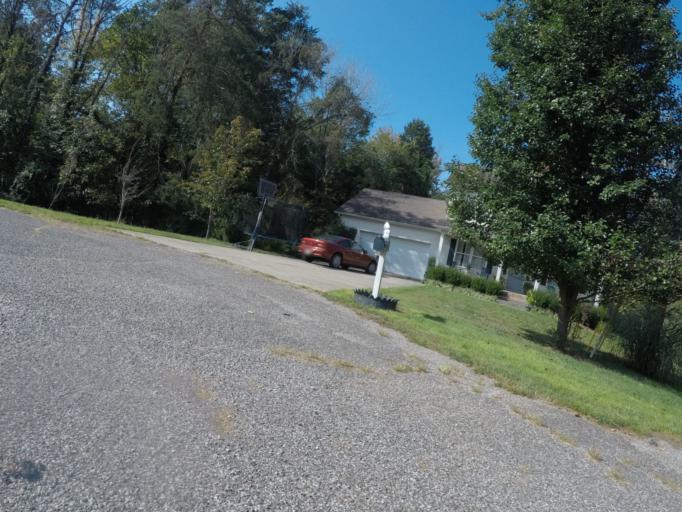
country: US
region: West Virginia
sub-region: Cabell County
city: Barboursville
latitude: 38.3648
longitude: -82.2739
